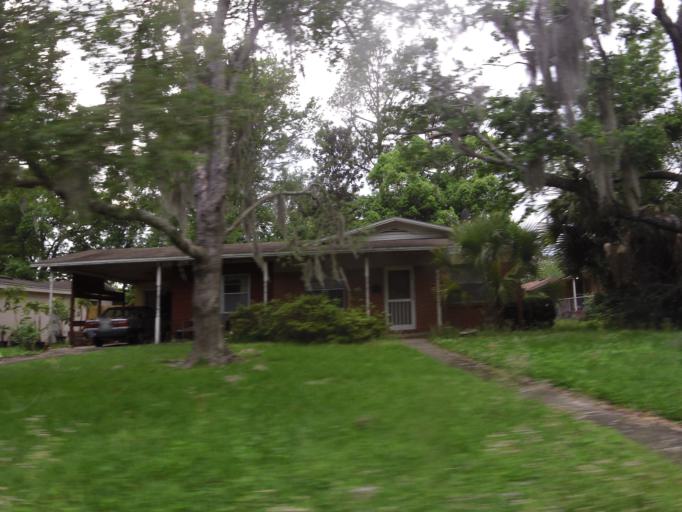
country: US
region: Florida
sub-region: Duval County
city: Jacksonville
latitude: 30.2950
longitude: -81.7353
